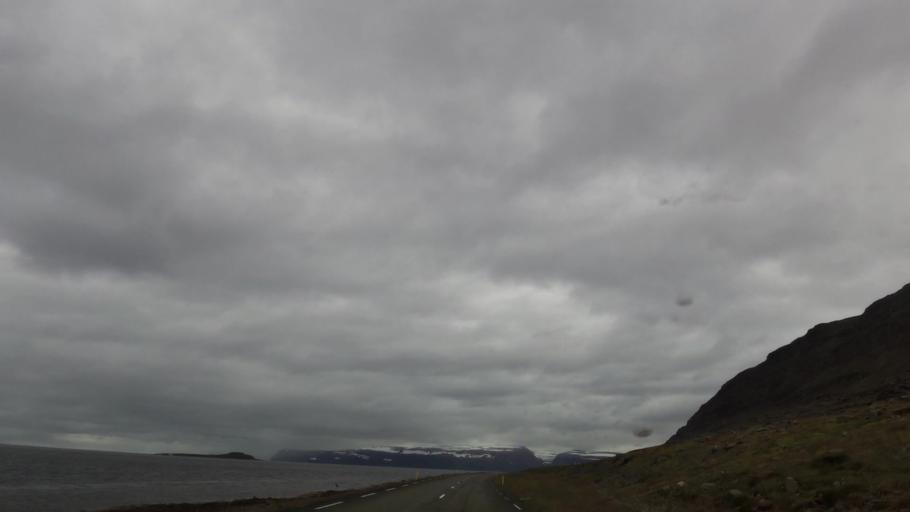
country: IS
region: Westfjords
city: Isafjoerdur
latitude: 66.0149
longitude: -22.7816
